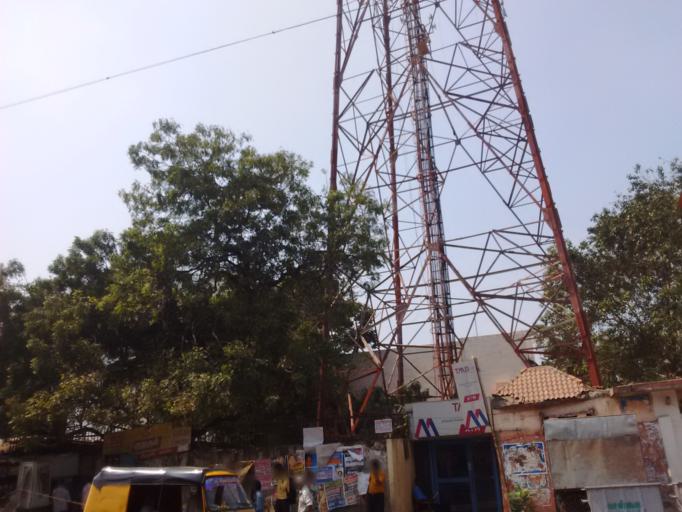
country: IN
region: Tamil Nadu
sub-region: Thiruvallur
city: Tiruvottiyur
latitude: 13.1729
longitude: 80.3055
